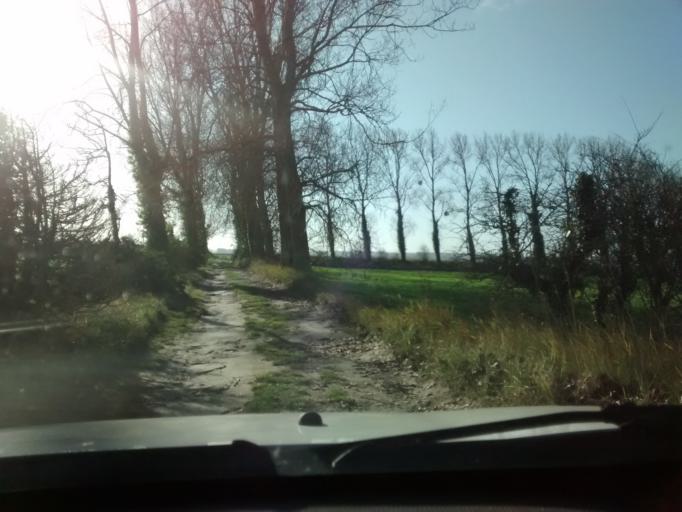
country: FR
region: Brittany
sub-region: Departement d'Ille-et-Vilaine
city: Roz-sur-Couesnon
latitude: 48.6280
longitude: -1.5342
